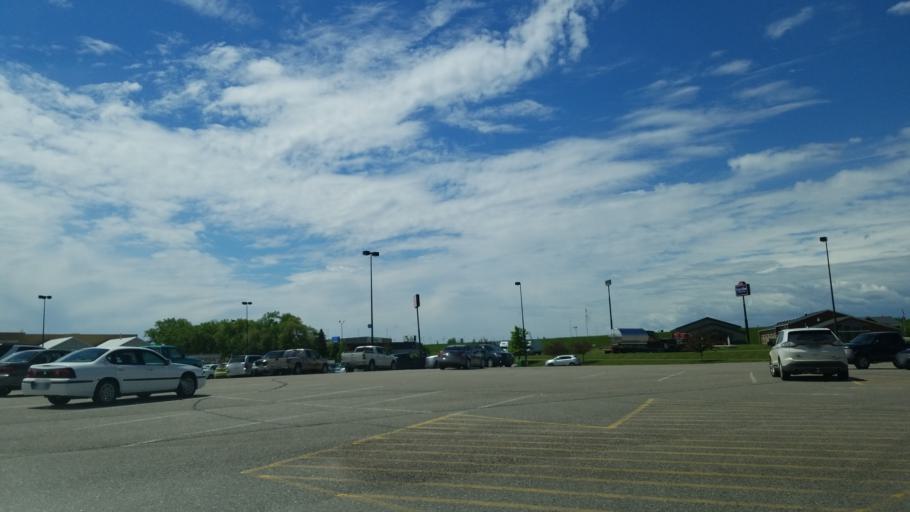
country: US
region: Minnesota
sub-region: Stearns County
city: Sauk Centre
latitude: 45.7225
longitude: -94.9474
